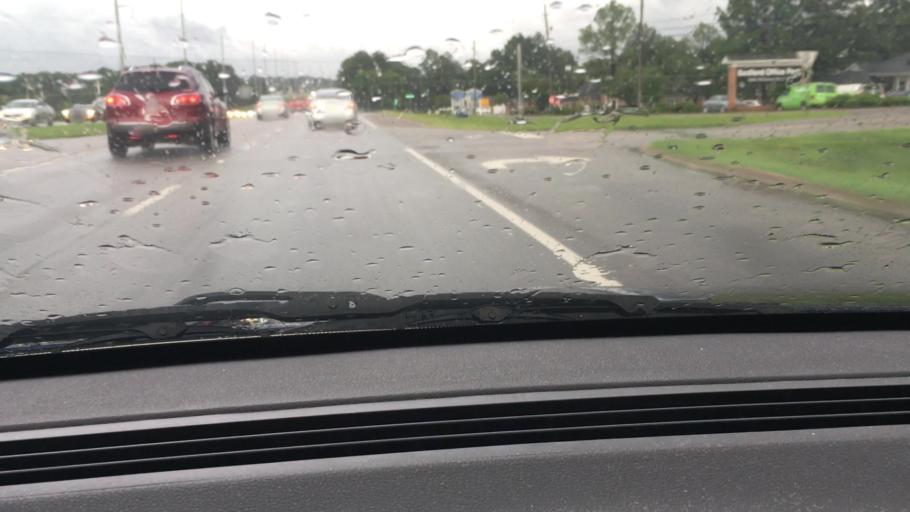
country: US
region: Alabama
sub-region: Tuscaloosa County
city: Northport
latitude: 33.2352
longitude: -87.5511
